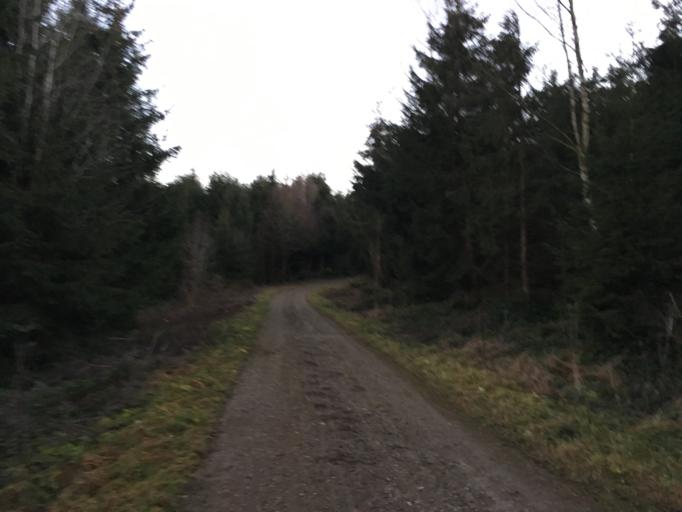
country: DE
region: Bavaria
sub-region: Swabia
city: Bohen
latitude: 47.8702
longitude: 10.2882
